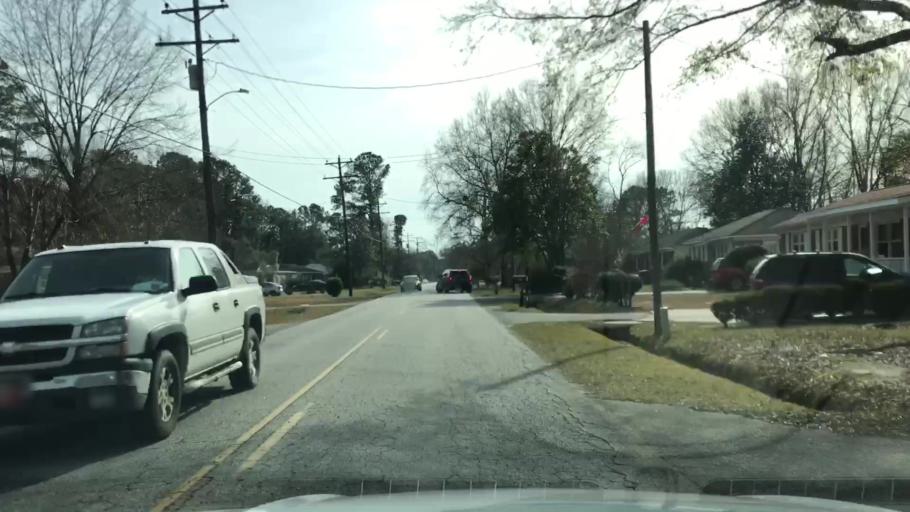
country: US
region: South Carolina
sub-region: Berkeley County
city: Goose Creek
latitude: 33.0199
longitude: -80.0289
